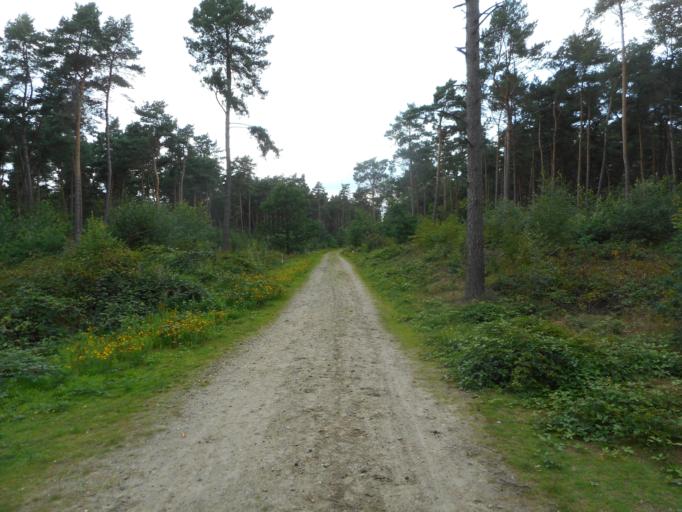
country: BE
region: Flanders
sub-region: Provincie Antwerpen
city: Lille
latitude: 51.2776
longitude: 4.8333
